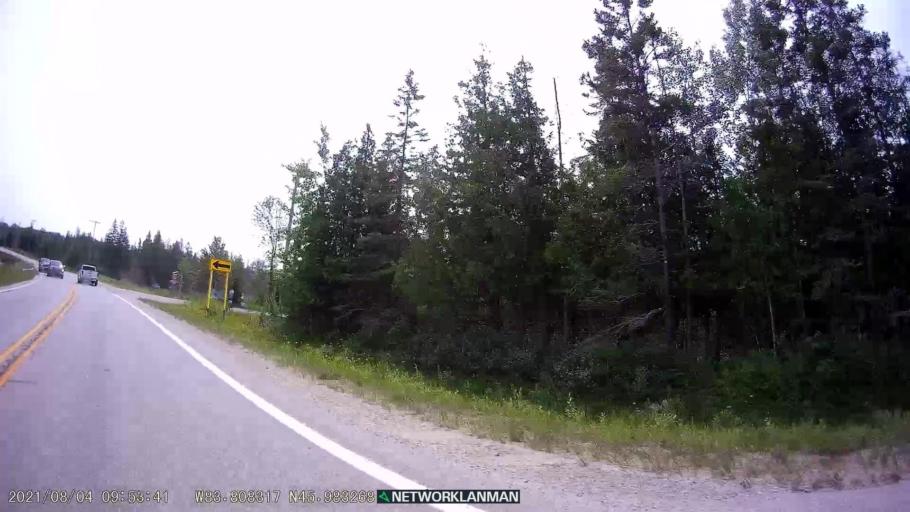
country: CA
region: Ontario
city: Thessalon
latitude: 45.9832
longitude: -83.8082
